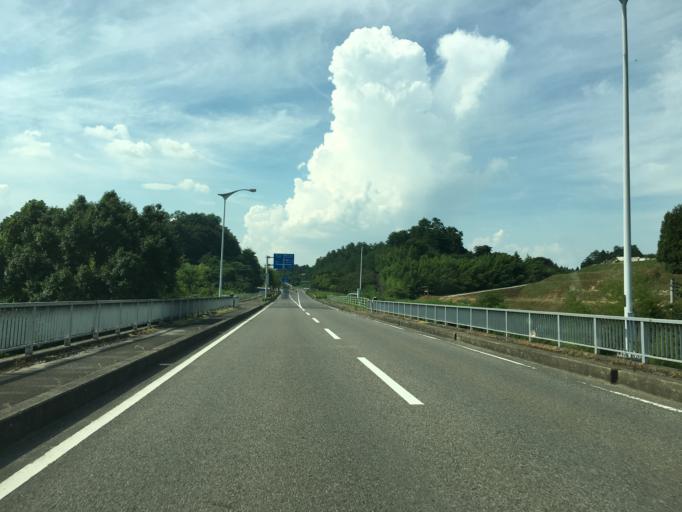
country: JP
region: Fukushima
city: Sukagawa
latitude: 37.2509
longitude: 140.4299
